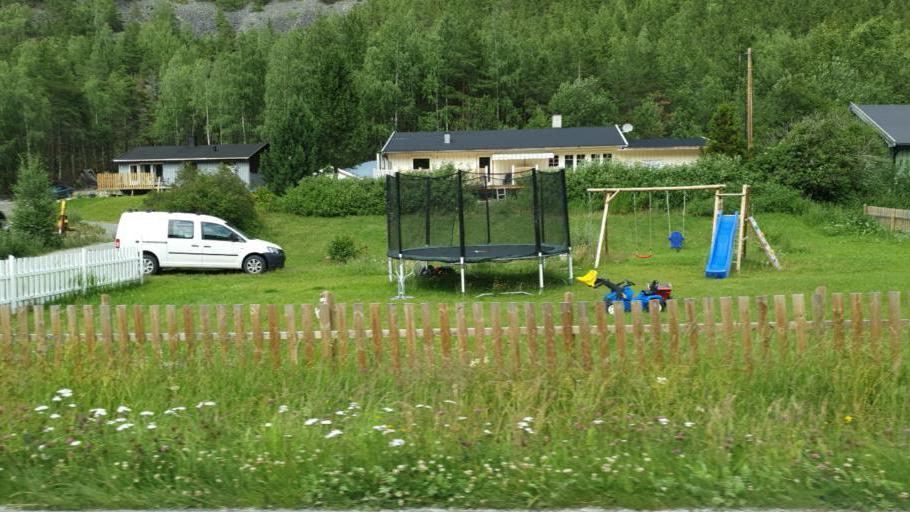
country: NO
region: Oppland
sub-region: Sel
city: Otta
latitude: 61.8435
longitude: 9.3771
